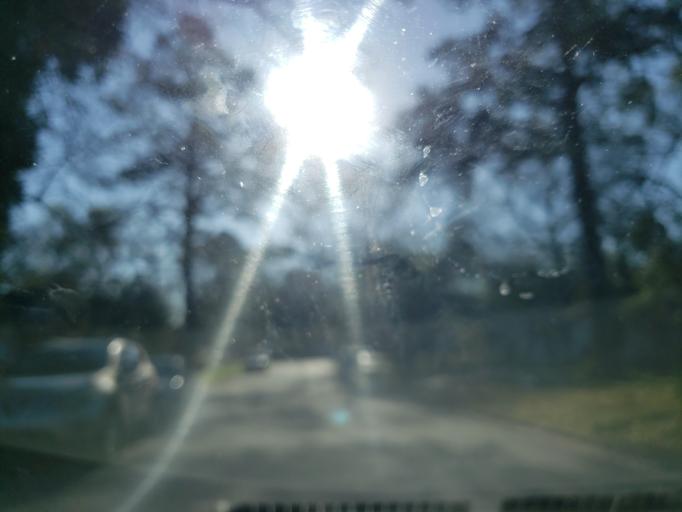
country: US
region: Georgia
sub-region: Chatham County
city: Thunderbolt
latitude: 32.0249
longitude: -81.0915
